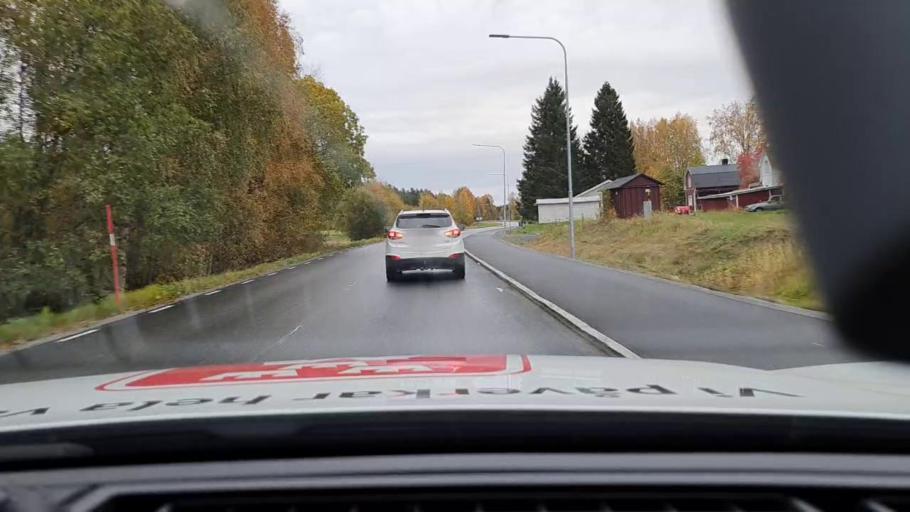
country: SE
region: Norrbotten
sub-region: Bodens Kommun
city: Saevast
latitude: 65.7727
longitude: 21.6994
